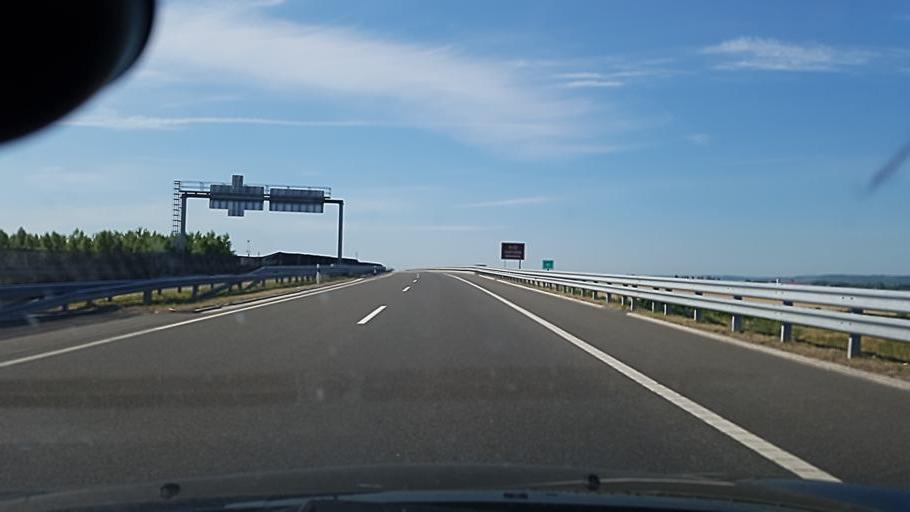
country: HU
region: Tolna
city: Szekszard
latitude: 46.3697
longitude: 18.7508
